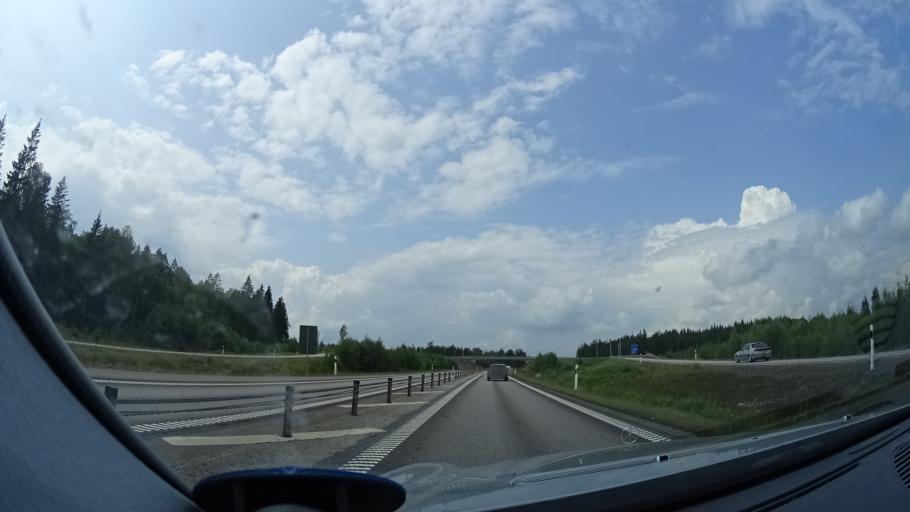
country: SE
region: Kalmar
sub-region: Nybro Kommun
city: Nybro
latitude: 56.7273
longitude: 15.8896
